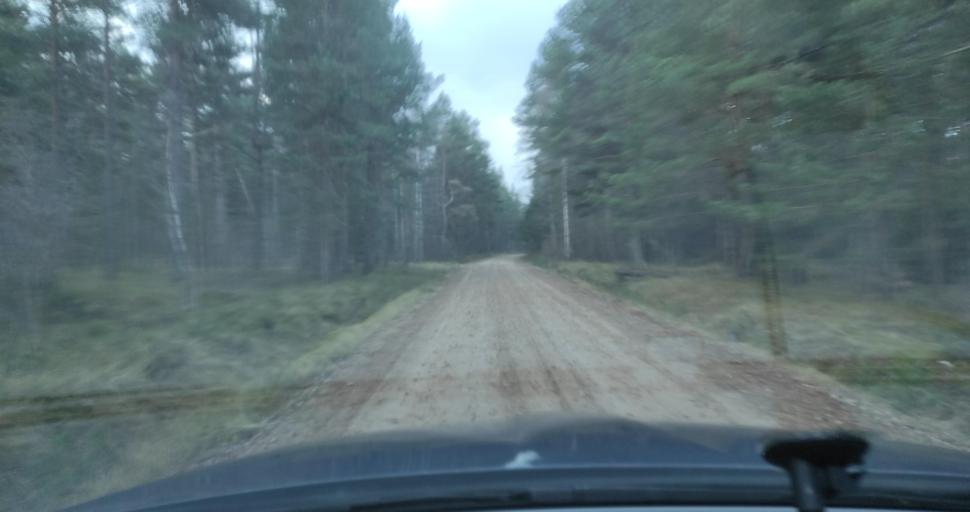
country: LV
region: Pavilostas
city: Pavilosta
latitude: 56.8283
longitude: 21.0705
